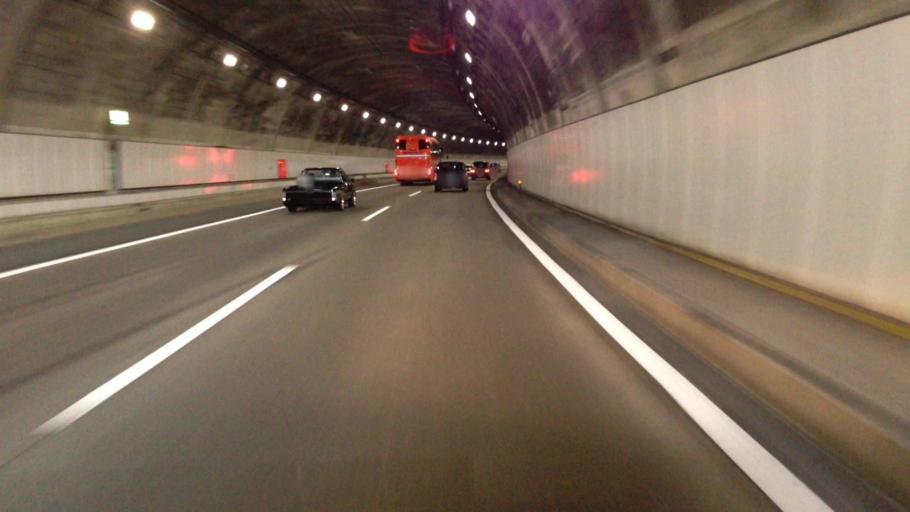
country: JP
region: Kanagawa
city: Zushi
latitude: 35.3045
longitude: 139.6102
